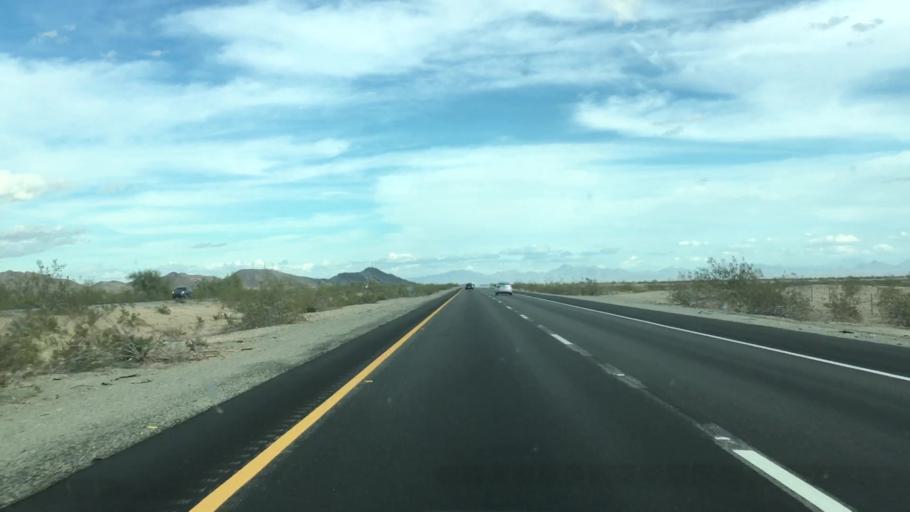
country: US
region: California
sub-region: Riverside County
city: Mesa Verde
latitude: 33.6097
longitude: -114.8155
